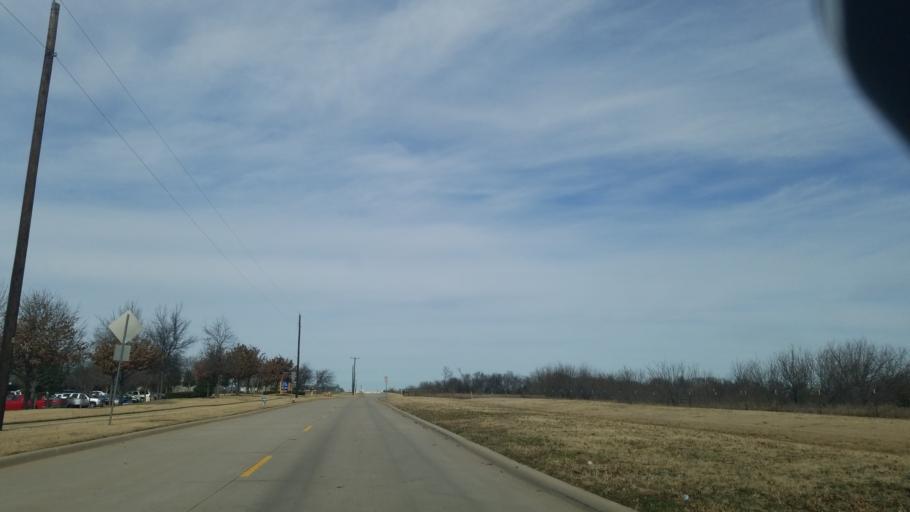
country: US
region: Texas
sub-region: Denton County
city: Denton
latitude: 33.1918
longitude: -97.1906
